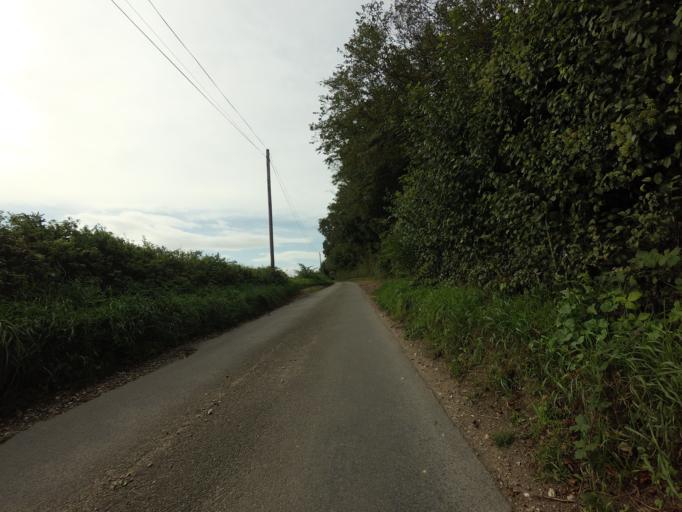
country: GB
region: England
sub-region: Norfolk
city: Wells-next-the-Sea
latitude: 52.9417
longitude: 0.7095
